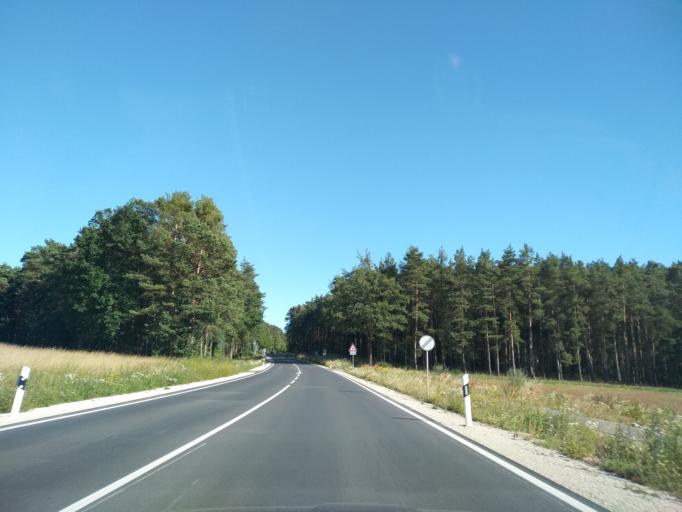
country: DE
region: Bavaria
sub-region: Regierungsbezirk Mittelfranken
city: Rottenbach
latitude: 49.6455
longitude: 10.9213
